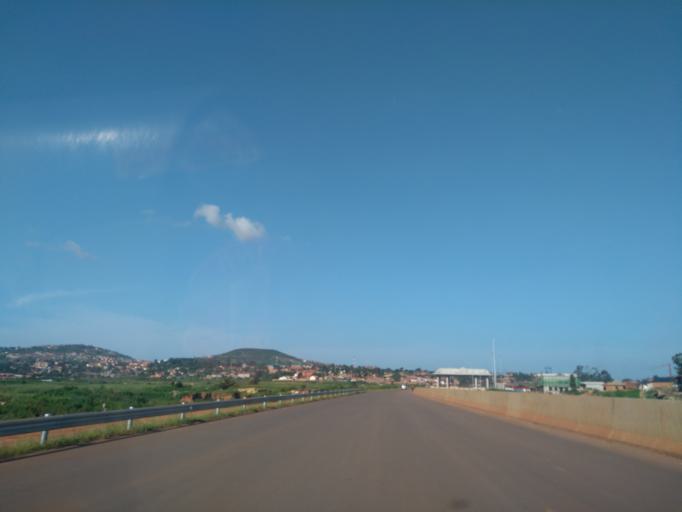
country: UG
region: Central Region
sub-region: Wakiso District
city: Kajansi
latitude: 0.2153
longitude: 32.5339
